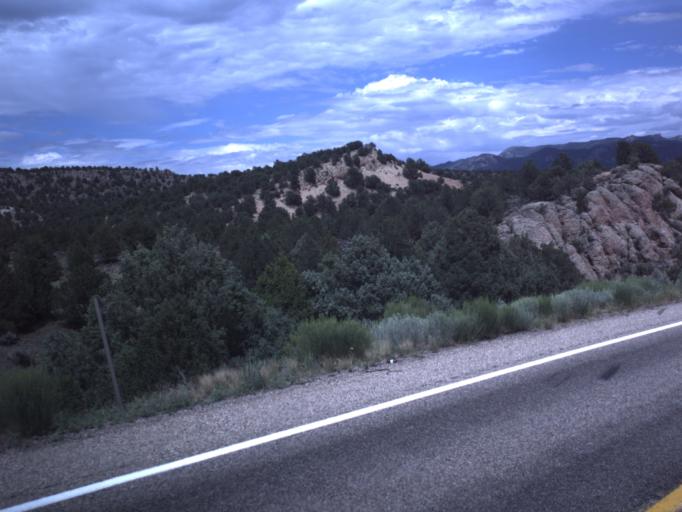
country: US
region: Utah
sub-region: Garfield County
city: Panguitch
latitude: 37.9719
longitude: -112.4473
